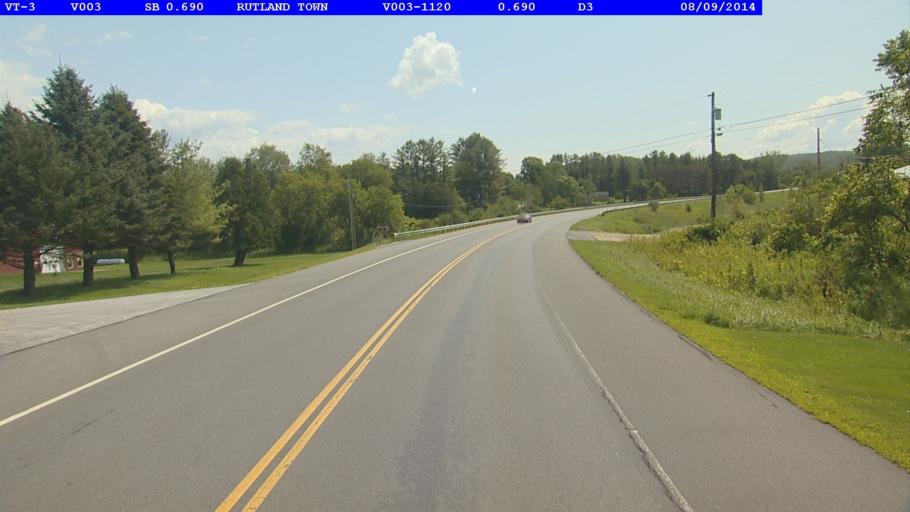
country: US
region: Vermont
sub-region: Rutland County
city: West Rutland
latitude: 43.6135
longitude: -73.0173
